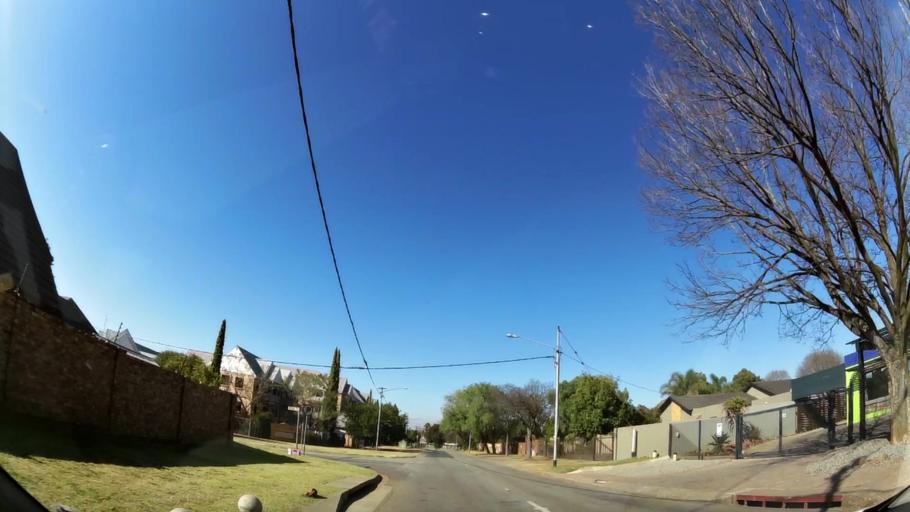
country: ZA
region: Gauteng
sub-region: City of Tshwane Metropolitan Municipality
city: Centurion
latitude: -25.8434
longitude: 28.2076
